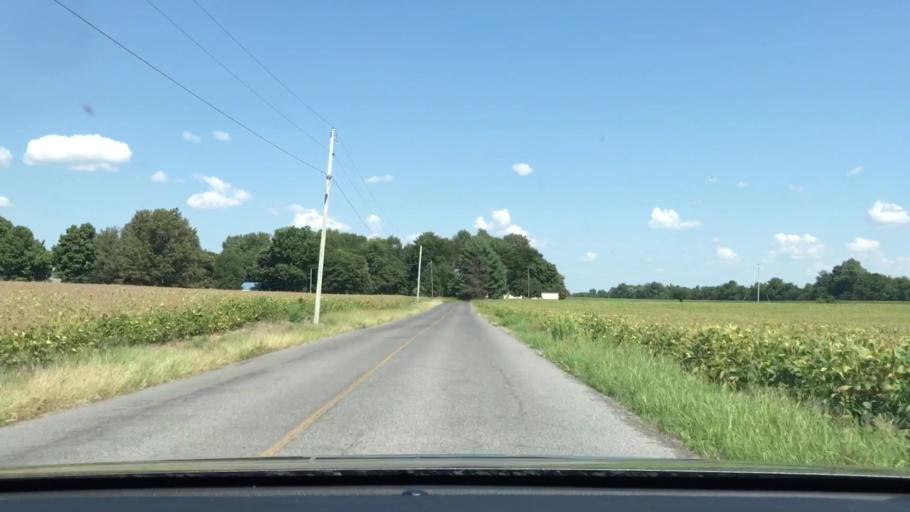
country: US
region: Kentucky
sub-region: Fulton County
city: Fulton
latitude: 36.5206
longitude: -88.9014
